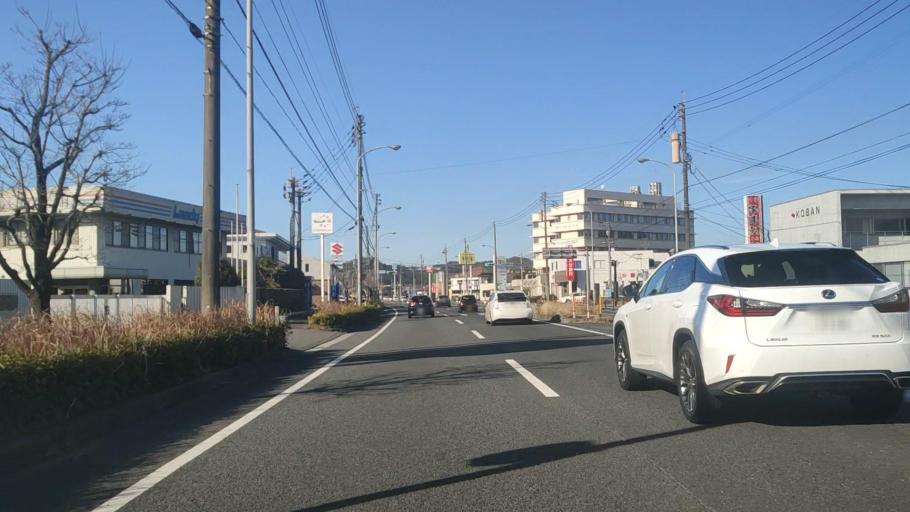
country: JP
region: Oita
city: Oita
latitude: 33.1529
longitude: 131.6561
